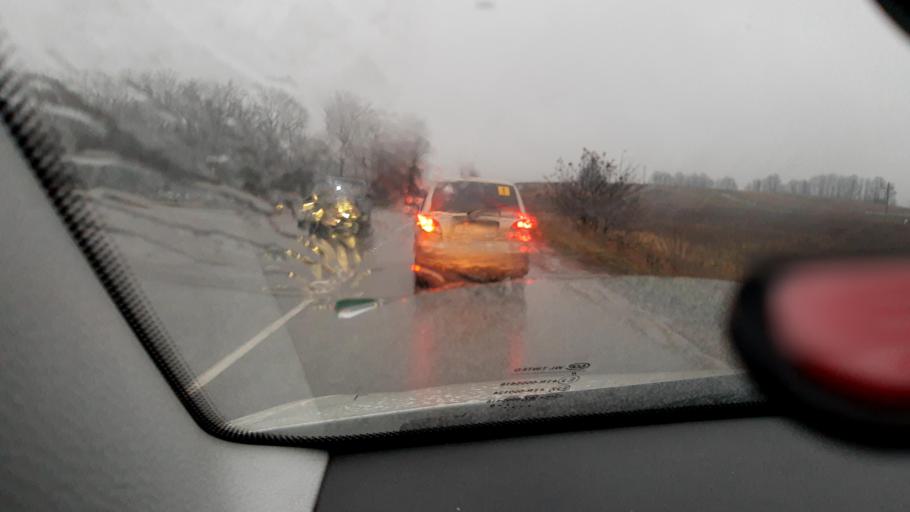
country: RU
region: Bashkortostan
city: Iglino
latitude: 54.9005
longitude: 56.1856
